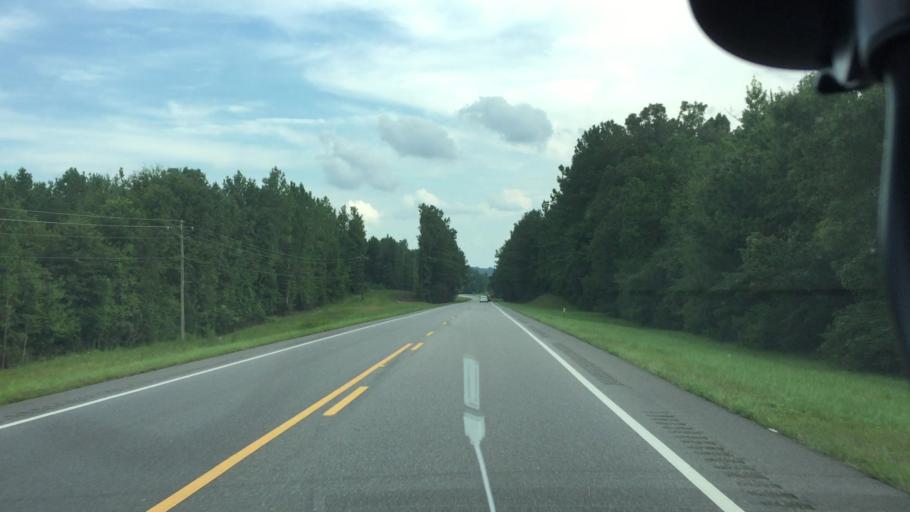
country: US
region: Alabama
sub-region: Coffee County
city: New Brockton
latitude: 31.4963
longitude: -85.9148
